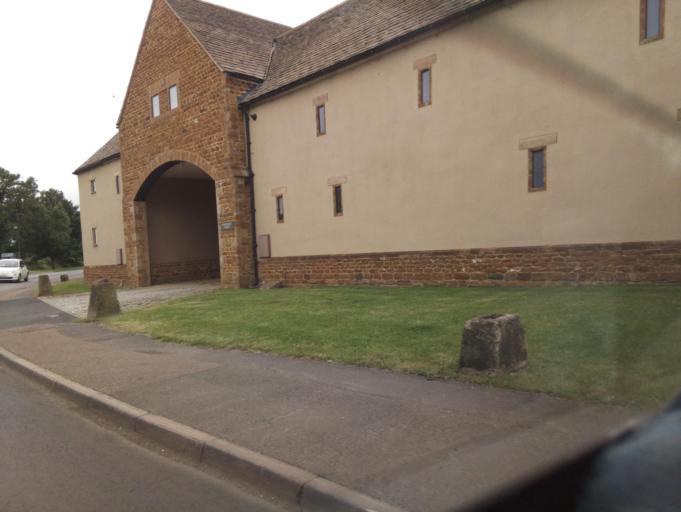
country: GB
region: England
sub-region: District of Rutland
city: Preston
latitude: 52.6117
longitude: -0.7130
